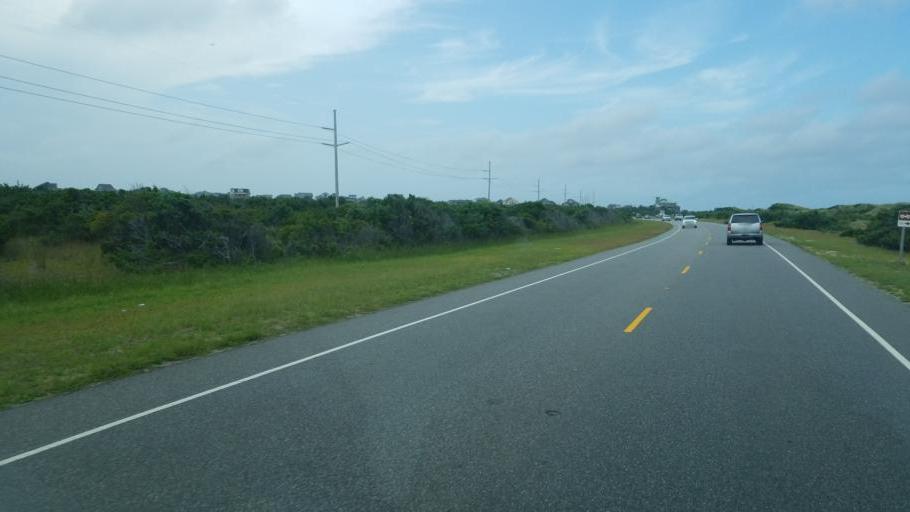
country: US
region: North Carolina
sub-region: Dare County
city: Buxton
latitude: 35.3174
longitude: -75.5100
